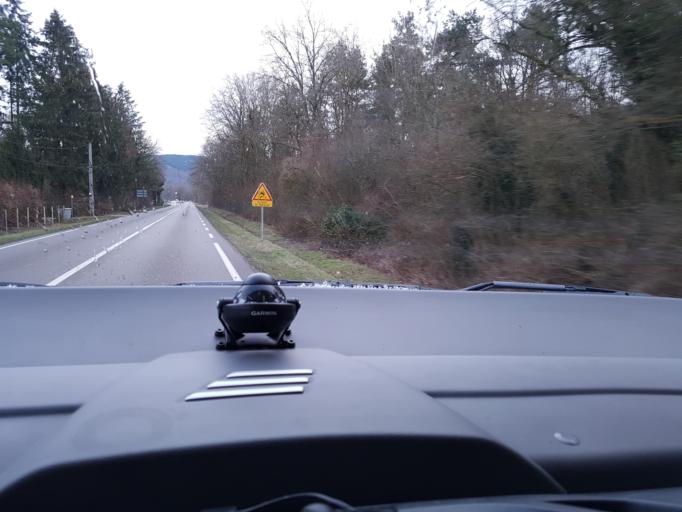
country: FR
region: Alsace
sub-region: Departement du Bas-Rhin
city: Chatenois
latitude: 48.2986
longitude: 7.3563
